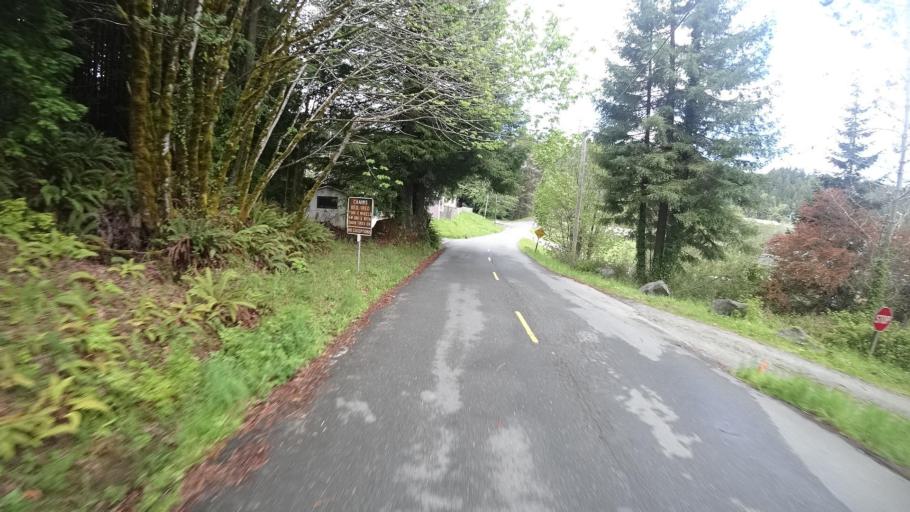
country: US
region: California
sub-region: Humboldt County
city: Blue Lake
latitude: 40.8701
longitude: -123.9582
